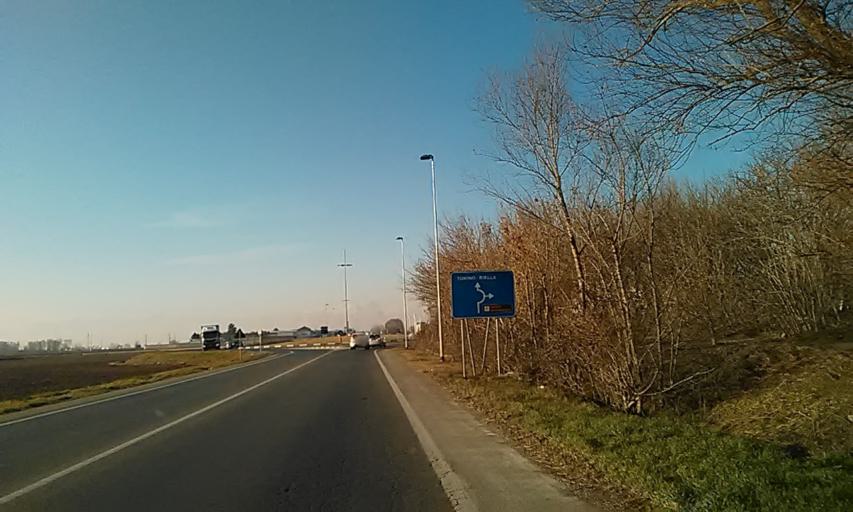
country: IT
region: Piedmont
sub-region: Provincia di Vercelli
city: Vercelli
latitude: 45.3159
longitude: 8.3952
